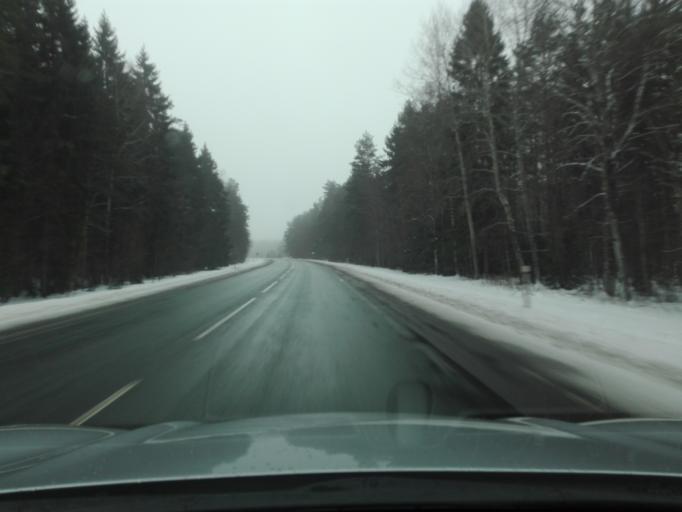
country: EE
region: Raplamaa
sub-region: Kohila vald
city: Kohila
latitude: 59.1664
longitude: 24.7714
